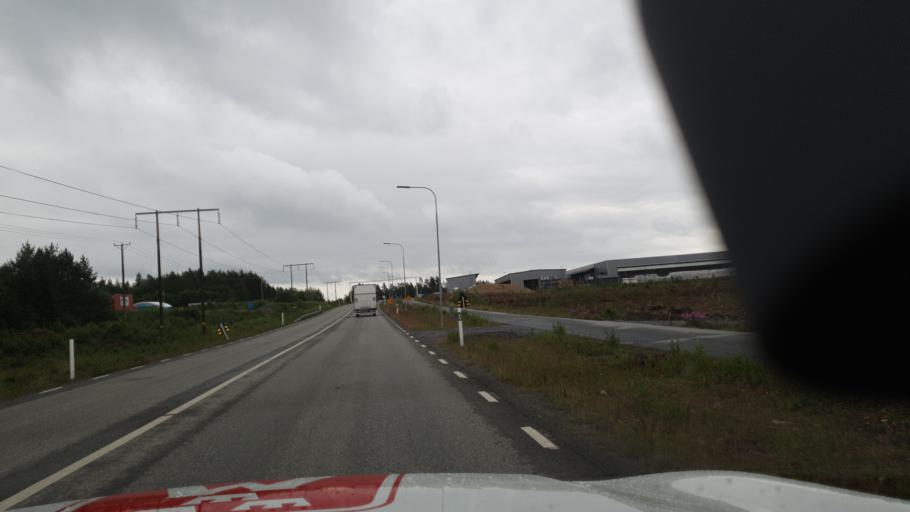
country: SE
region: Vaesterbotten
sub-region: Umea Kommun
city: Roback
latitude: 63.8494
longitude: 20.1480
